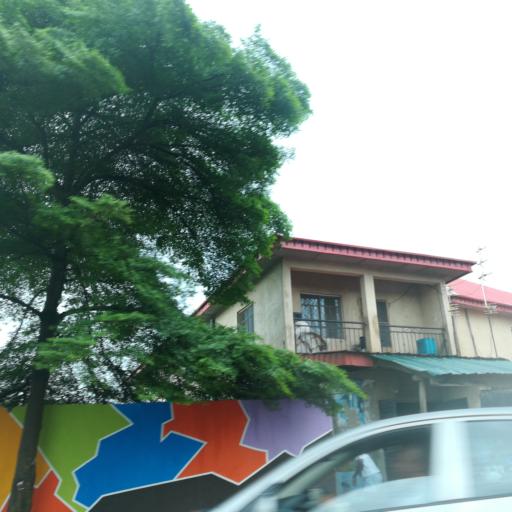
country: NG
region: Lagos
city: Oshodi
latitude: 6.5558
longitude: 3.3448
